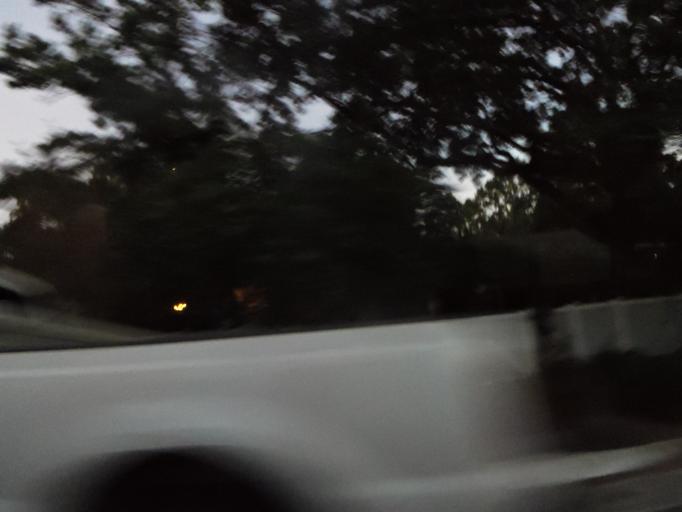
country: US
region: Florida
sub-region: Duval County
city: Jacksonville
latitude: 30.2869
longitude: -81.7110
